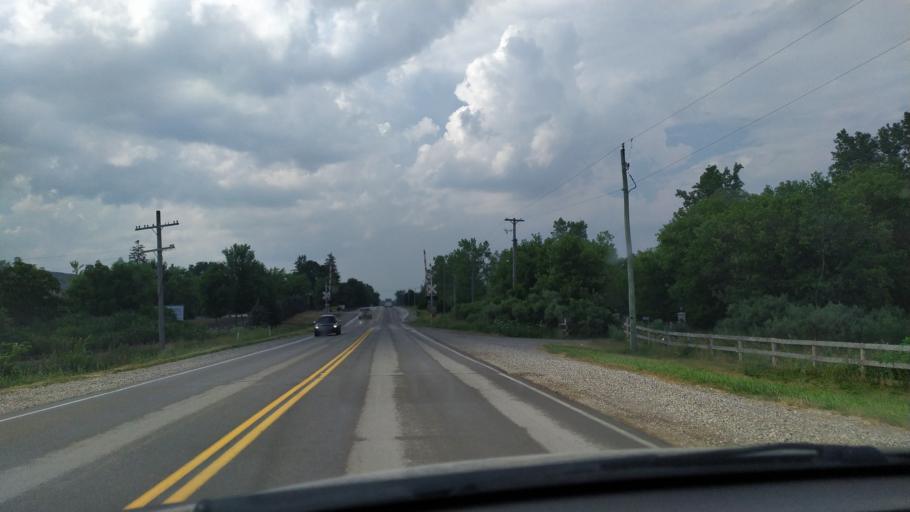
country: CA
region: Ontario
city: Dorchester
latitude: 43.0844
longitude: -81.1479
